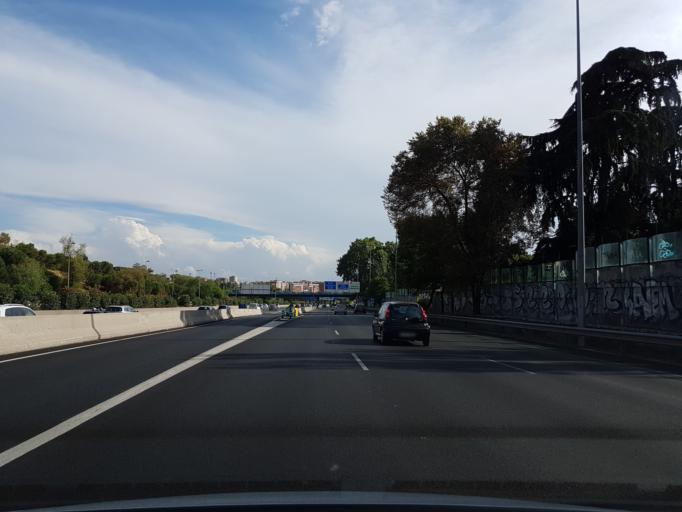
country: ES
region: Madrid
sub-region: Provincia de Madrid
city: Moratalaz
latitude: 40.4244
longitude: -3.6598
